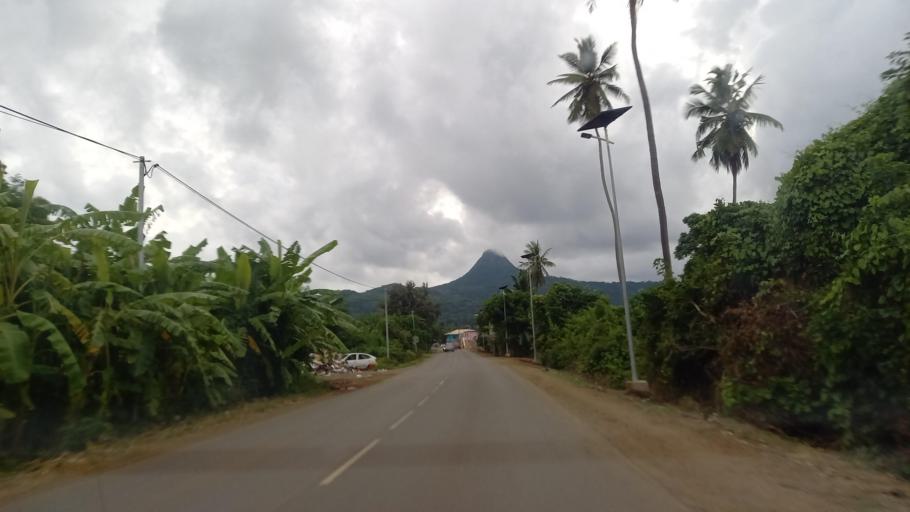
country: YT
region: Chirongui
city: Chirongui
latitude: -12.9258
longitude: 45.1546
